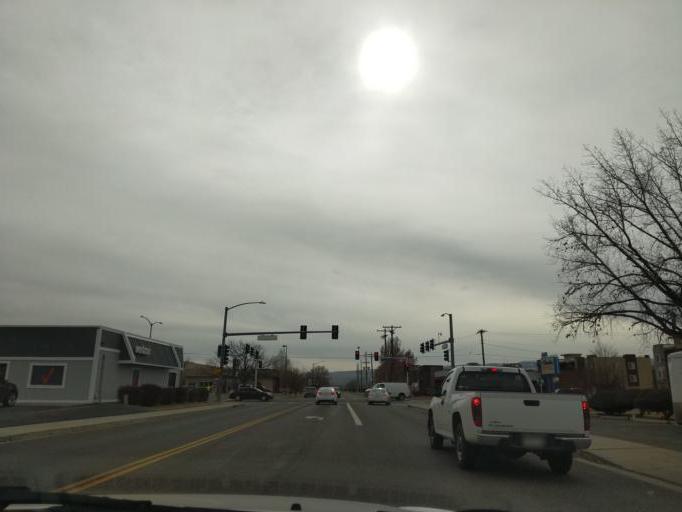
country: US
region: Colorado
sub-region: Mesa County
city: Grand Junction
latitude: 39.0780
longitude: -108.5292
